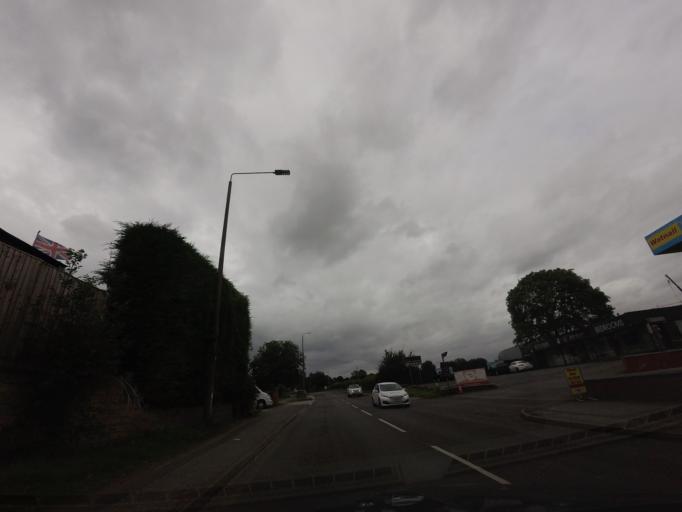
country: GB
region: England
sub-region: Nottinghamshire
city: Kimberley
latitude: 53.0036
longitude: -1.2500
